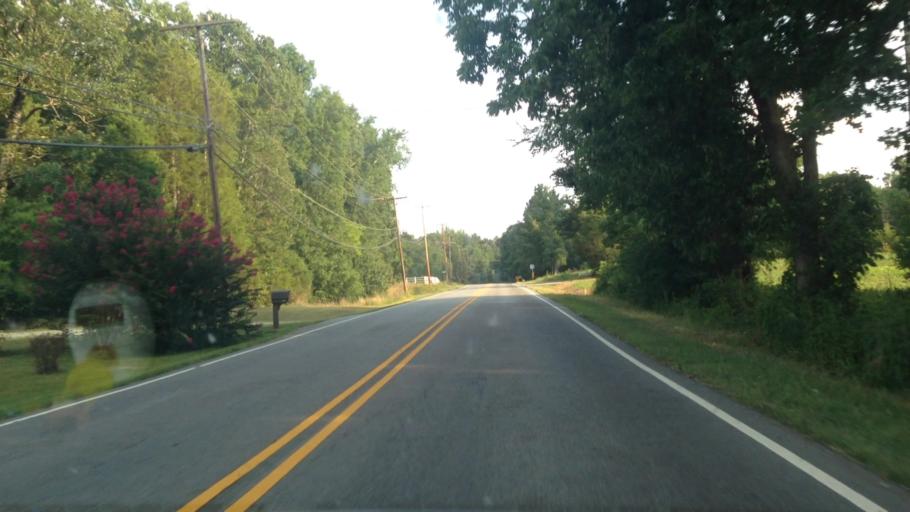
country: US
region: North Carolina
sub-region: Guilford County
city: High Point
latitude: 35.9960
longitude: -80.0627
